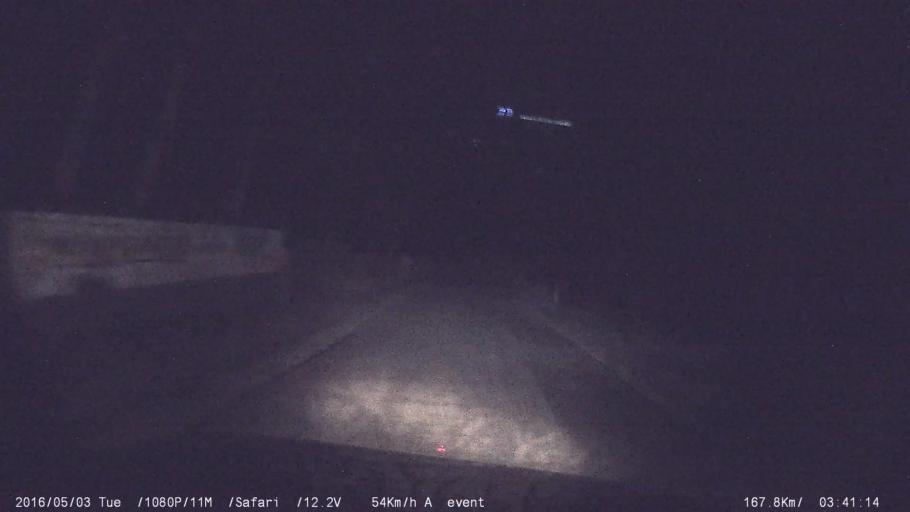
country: IN
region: Kerala
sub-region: Kottayam
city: Palackattumala
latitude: 9.7672
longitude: 76.6102
